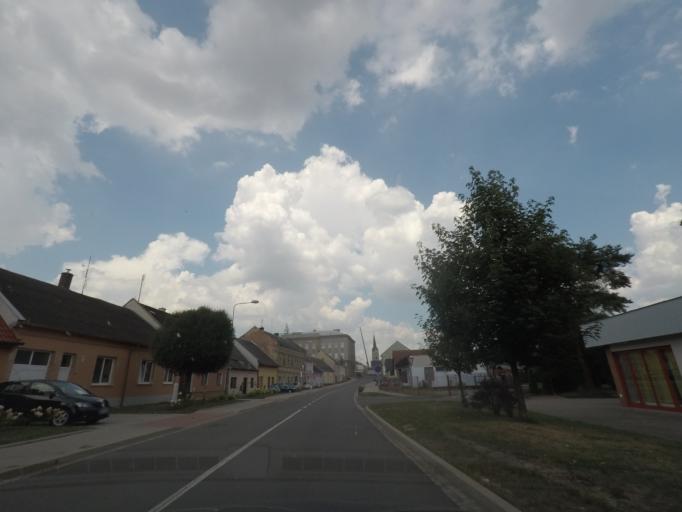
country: CZ
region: Olomoucky
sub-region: Okres Sumperk
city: Mohelnice
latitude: 49.7728
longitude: 16.9180
